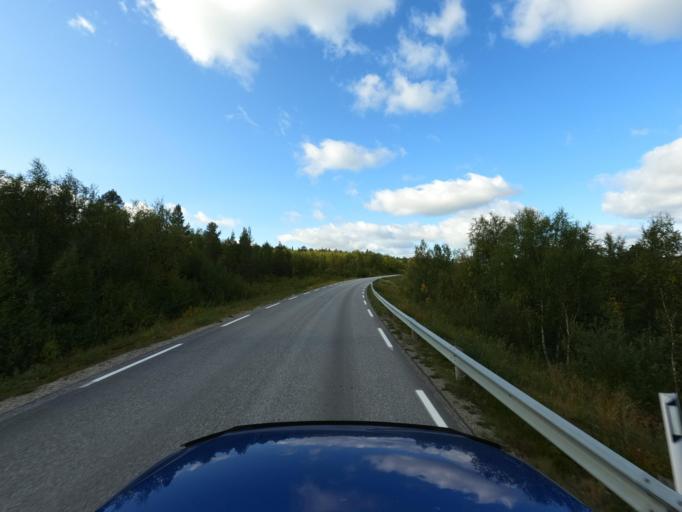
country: NO
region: Finnmark Fylke
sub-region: Karasjok
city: Karasjohka
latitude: 69.4282
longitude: 25.7580
